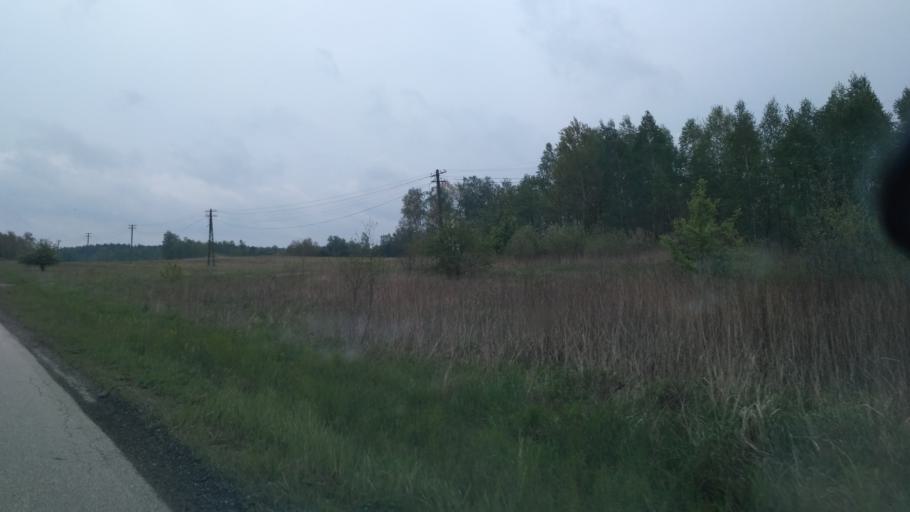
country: PL
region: Subcarpathian Voivodeship
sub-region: Powiat ropczycko-sedziszowski
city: Sedziszow Malopolski
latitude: 50.1146
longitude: 21.7462
